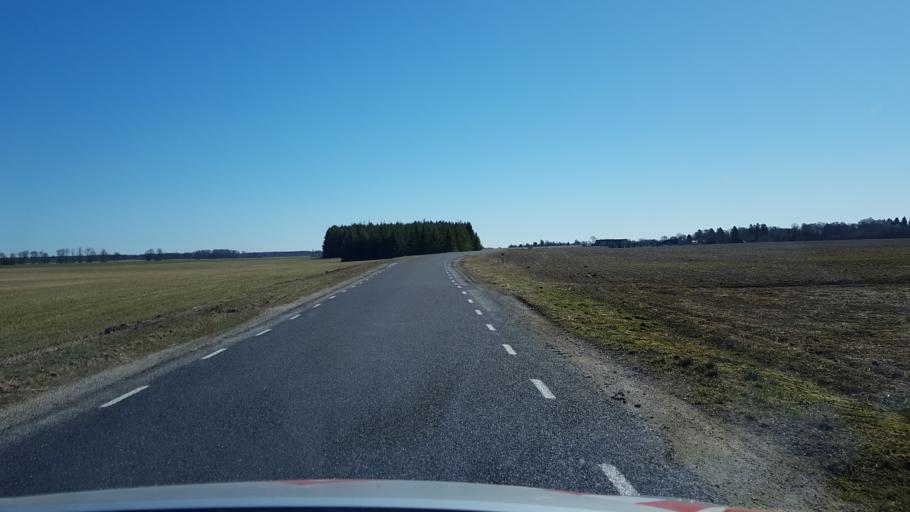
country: EE
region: Laeaene-Virumaa
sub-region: Haljala vald
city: Haljala
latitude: 59.4406
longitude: 26.1572
